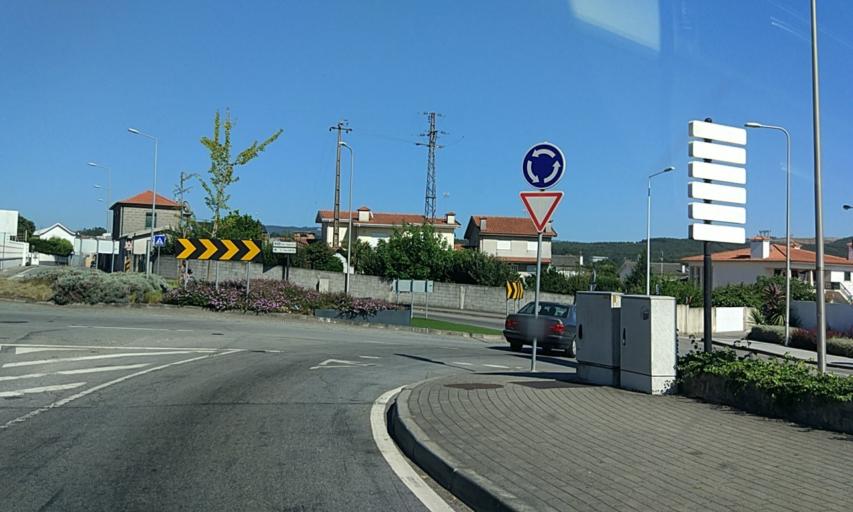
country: PT
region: Porto
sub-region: Trofa
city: Bougado
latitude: 41.3408
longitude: -8.5439
